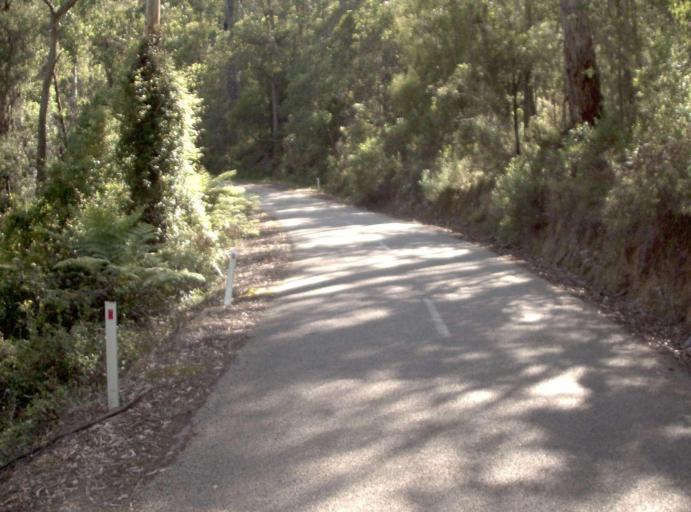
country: AU
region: Victoria
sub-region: East Gippsland
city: Lakes Entrance
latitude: -37.4377
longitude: 148.5924
